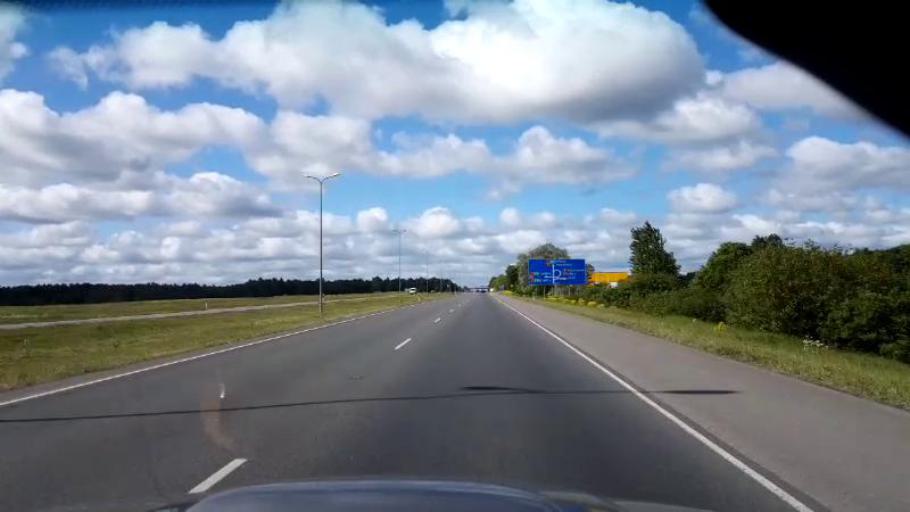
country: EE
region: Harju
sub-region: Saue linn
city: Saue
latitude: 59.3206
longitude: 24.5857
